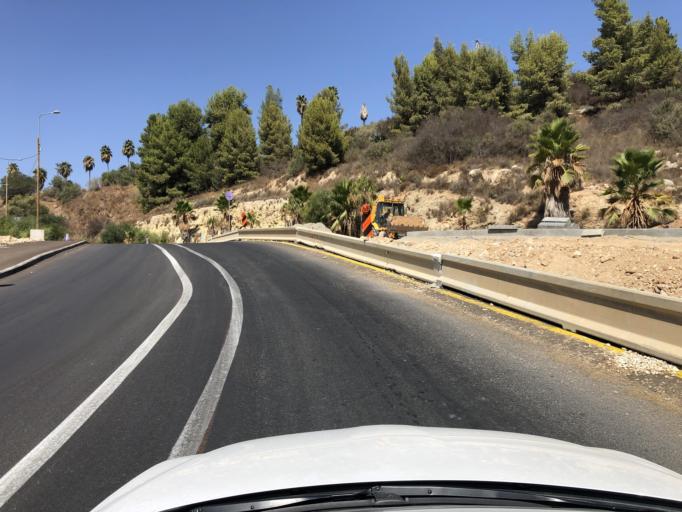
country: PS
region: West Bank
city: An Nabi Ilyas
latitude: 32.1718
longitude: 35.0062
